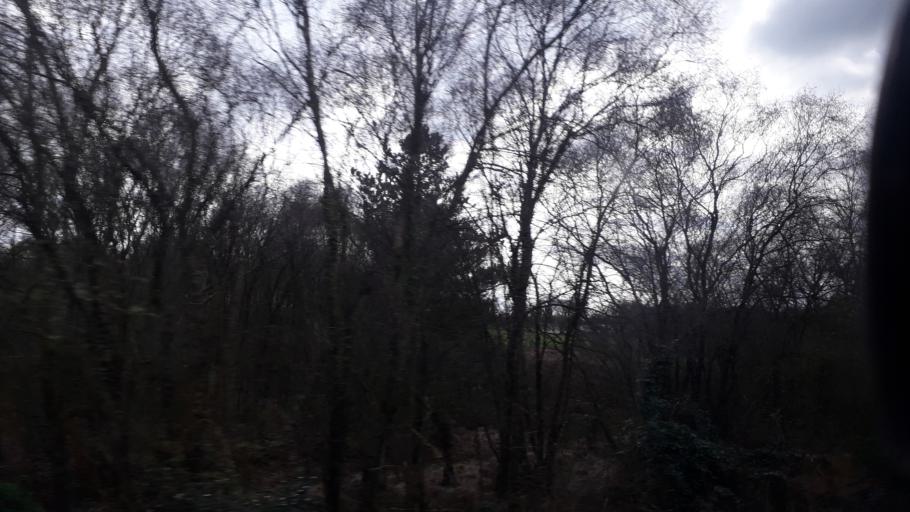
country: IE
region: Leinster
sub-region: An Iarmhi
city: Rochfortbridge
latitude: 53.4961
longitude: -7.2374
